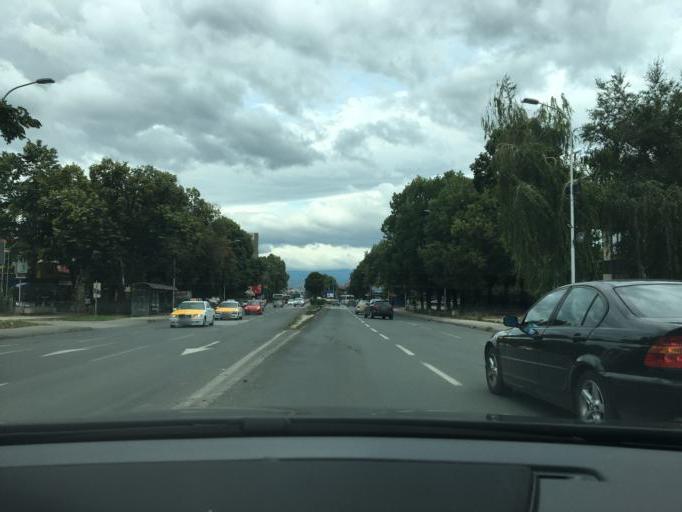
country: MK
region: Karpos
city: Skopje
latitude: 41.9958
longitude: 21.4408
